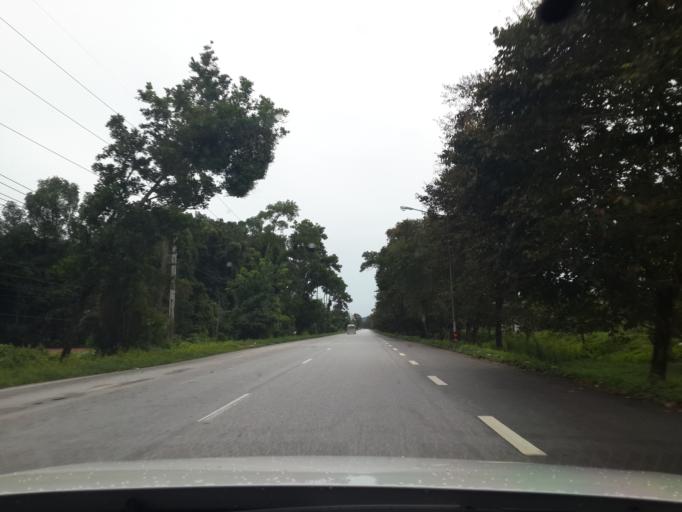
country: TH
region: Songkhla
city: Chana
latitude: 6.9189
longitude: 100.7469
